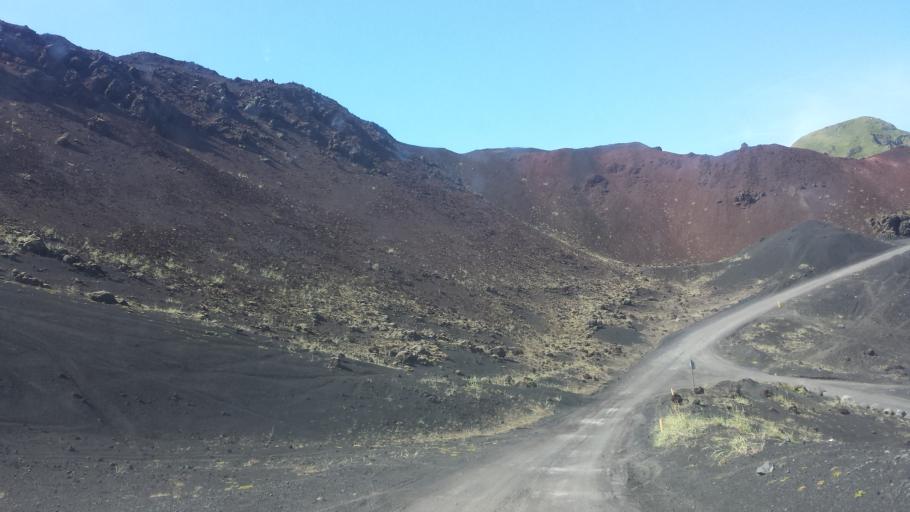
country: IS
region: South
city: Vestmannaeyjar
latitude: 63.4401
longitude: -20.2347
